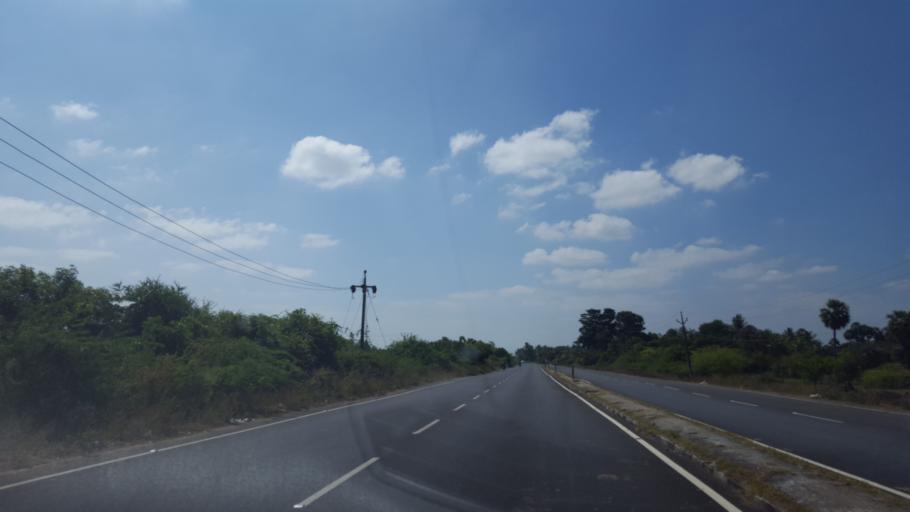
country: IN
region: Tamil Nadu
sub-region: Kancheepuram
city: Mamallapuram
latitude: 12.6865
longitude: 80.1798
